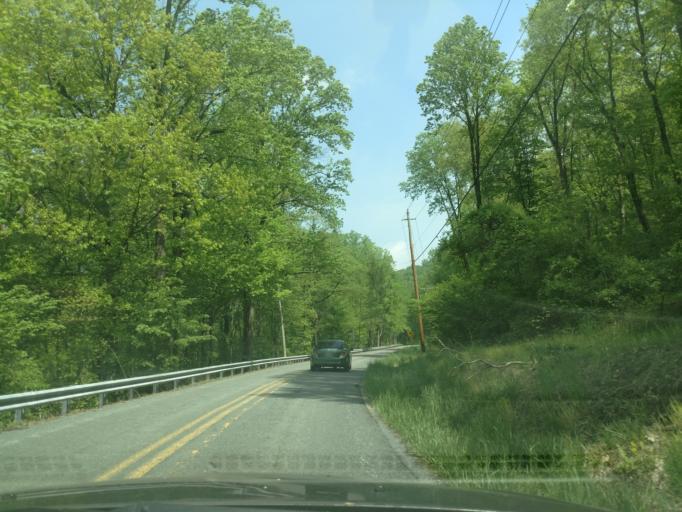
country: US
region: Pennsylvania
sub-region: Berks County
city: Birdsboro
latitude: 40.2385
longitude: -75.8356
